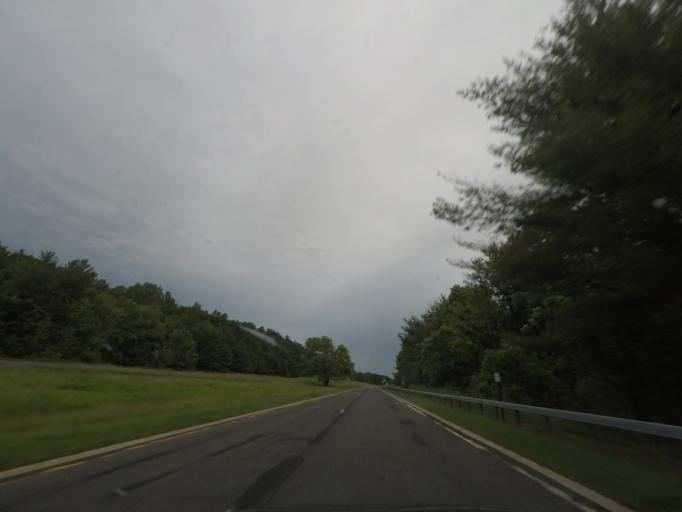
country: US
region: New York
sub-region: Columbia County
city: Chatham
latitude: 42.4074
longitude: -73.5489
